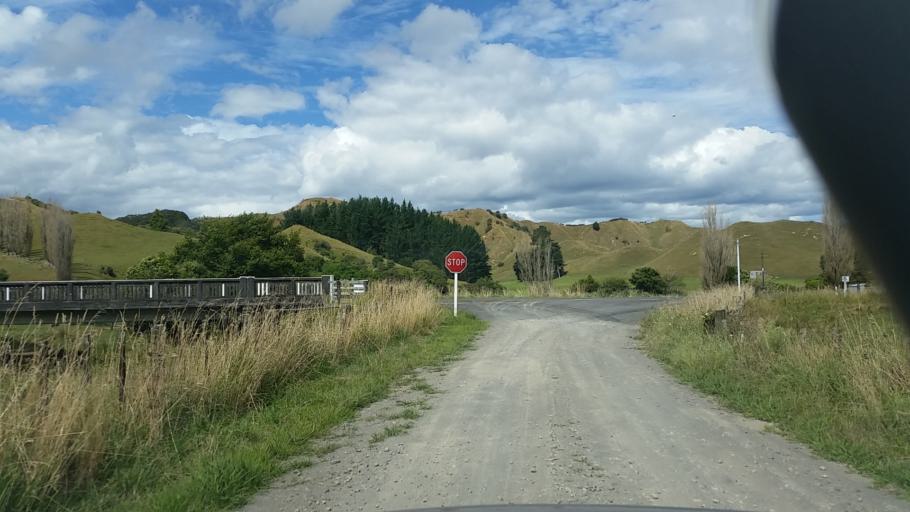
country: NZ
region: Taranaki
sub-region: South Taranaki District
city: Eltham
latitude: -39.2619
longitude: 174.5675
